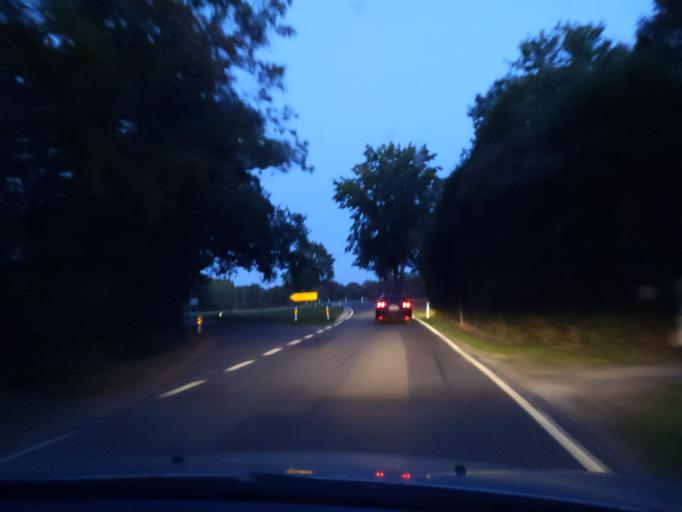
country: DE
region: Saxony
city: Grossdubrau
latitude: 51.2866
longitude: 14.4826
